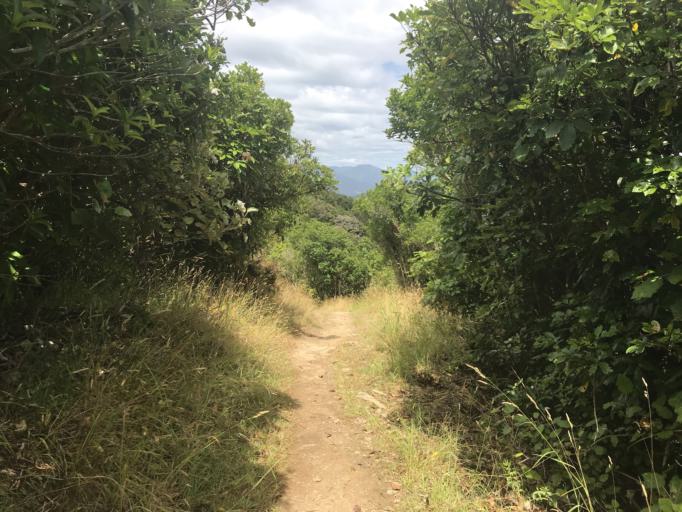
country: NZ
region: Marlborough
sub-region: Marlborough District
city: Picton
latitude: -41.2118
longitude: 174.0120
